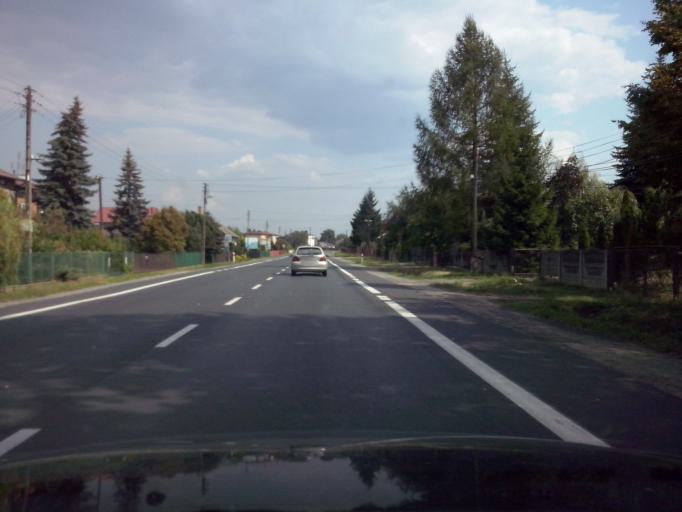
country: PL
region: Subcarpathian Voivodeship
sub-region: Powiat nizanski
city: Raclawice
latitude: 50.5162
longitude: 22.1577
